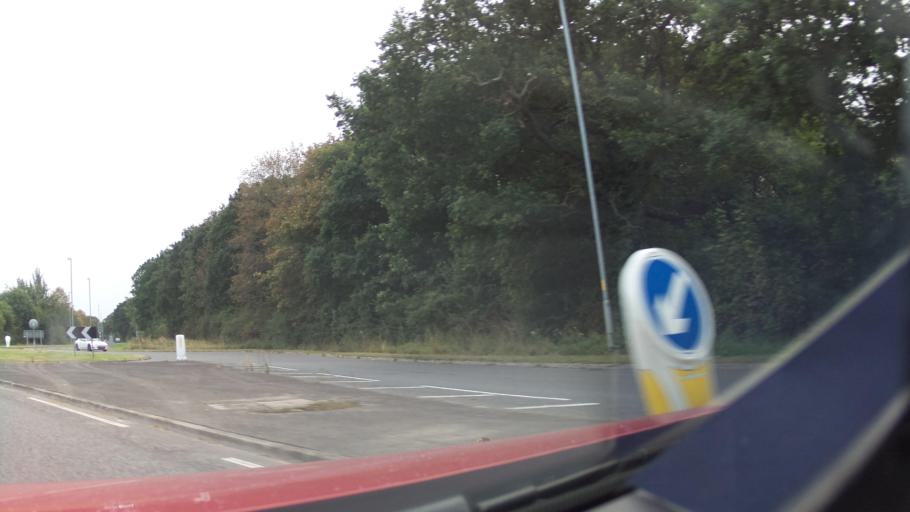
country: GB
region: England
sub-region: Nottinghamshire
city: South Collingham
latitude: 53.1491
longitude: -0.6698
